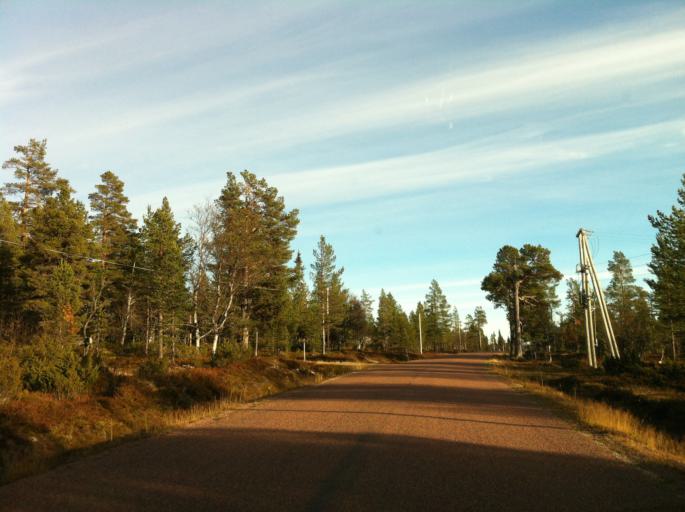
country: NO
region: Hedmark
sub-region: Engerdal
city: Engerdal
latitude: 62.0823
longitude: 12.1298
